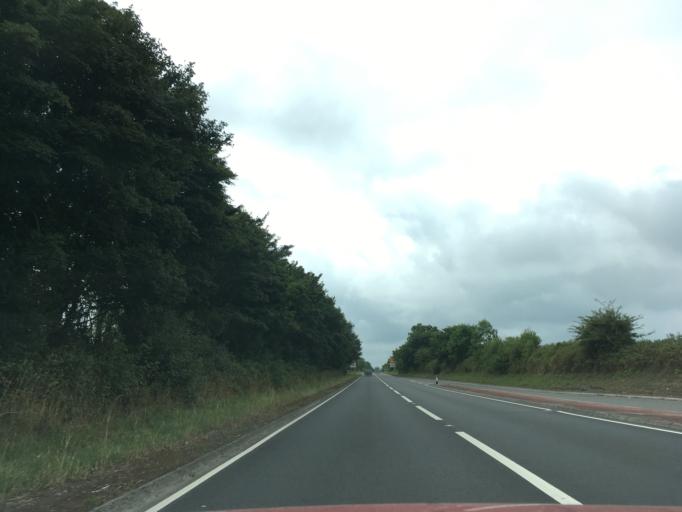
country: GB
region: Wales
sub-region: Carmarthenshire
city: Llanddowror
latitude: 51.8228
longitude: -4.5318
